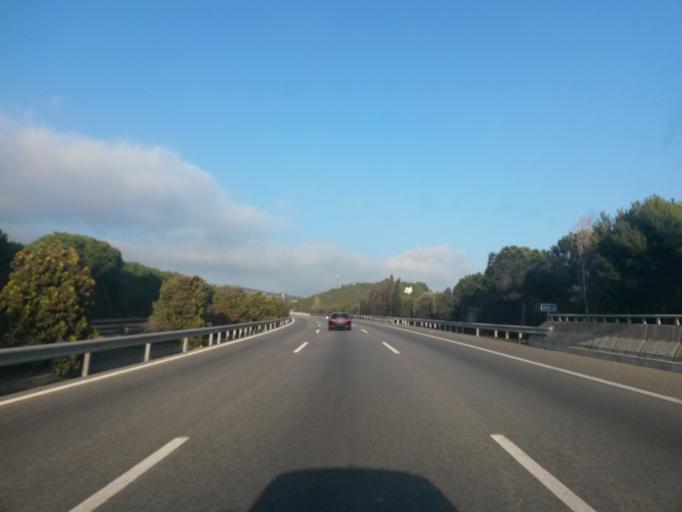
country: ES
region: Catalonia
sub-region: Provincia de Barcelona
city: Sant Andreu de Llavaneres
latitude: 41.5664
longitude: 2.4974
